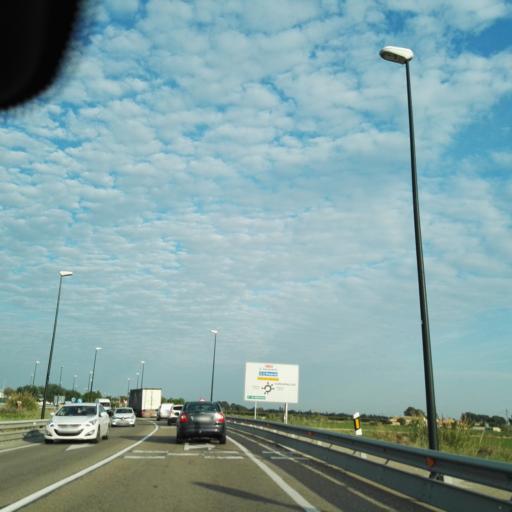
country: ES
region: Aragon
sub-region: Provincia de Zaragoza
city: Utebo
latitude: 41.6646
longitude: -0.9966
